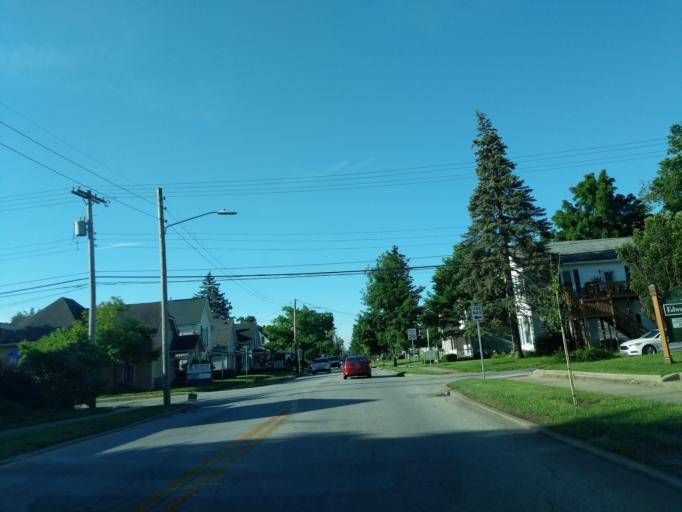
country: US
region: Indiana
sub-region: Hancock County
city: Greenfield
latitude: 39.7925
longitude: -85.7697
